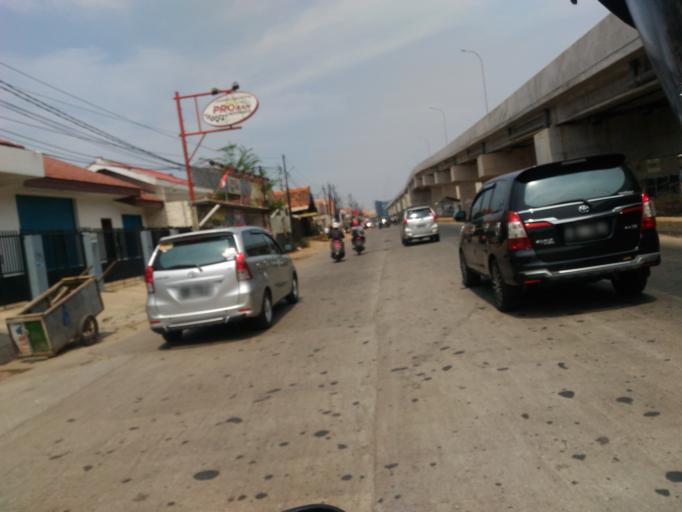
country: ID
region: Jakarta Raya
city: Jakarta
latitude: -6.2395
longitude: 106.8841
